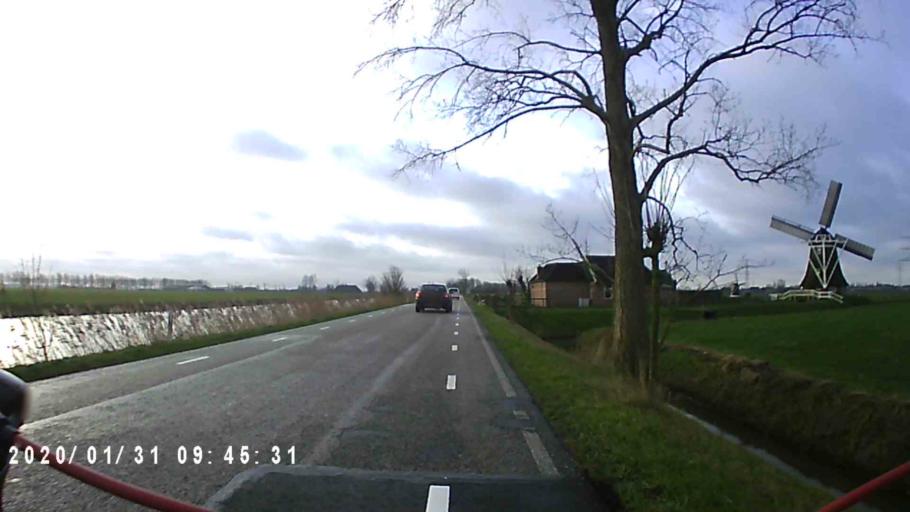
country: NL
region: Groningen
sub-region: Gemeente Zuidhorn
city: Aduard
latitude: 53.2690
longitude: 6.4835
